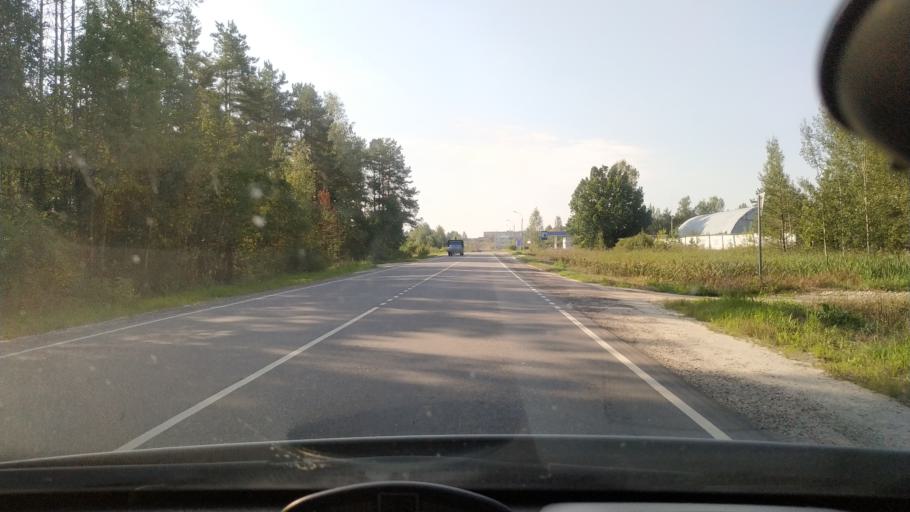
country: RU
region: Moskovskaya
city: Dmitrovskiy Pogost
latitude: 55.3242
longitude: 39.8254
